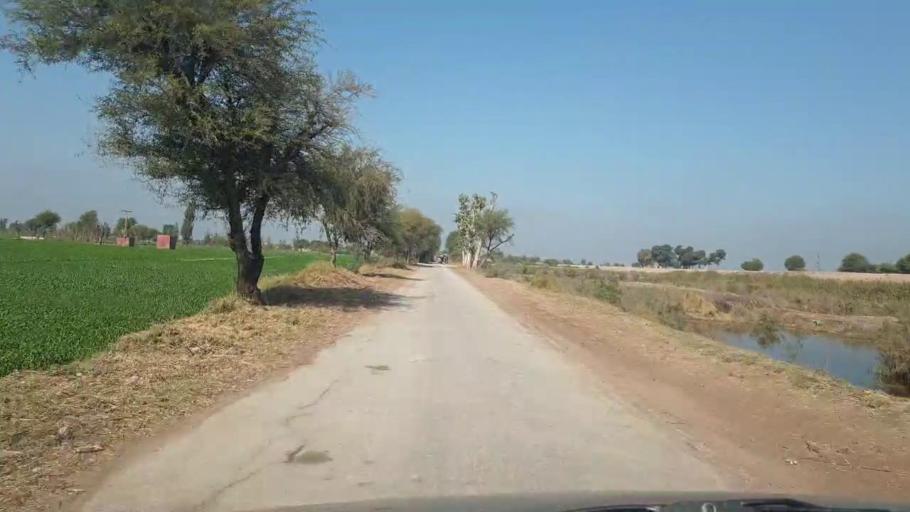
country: PK
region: Sindh
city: Shahdadpur
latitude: 25.8837
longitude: 68.5443
